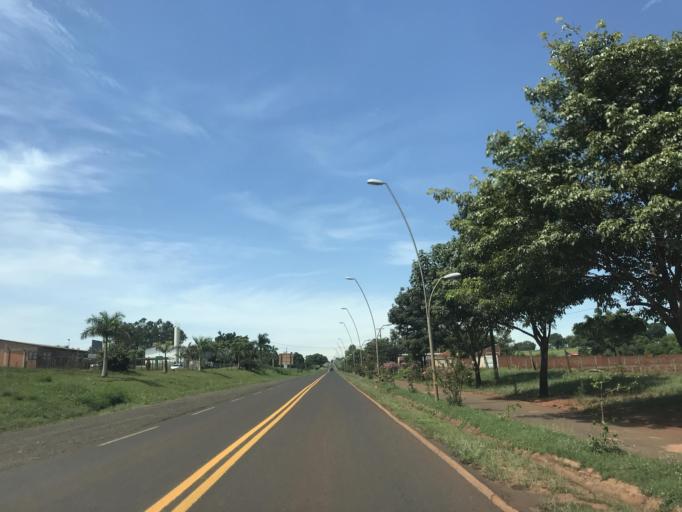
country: BR
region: Parana
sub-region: Terra Rica
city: Terra Rica
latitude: -22.7407
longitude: -52.6248
